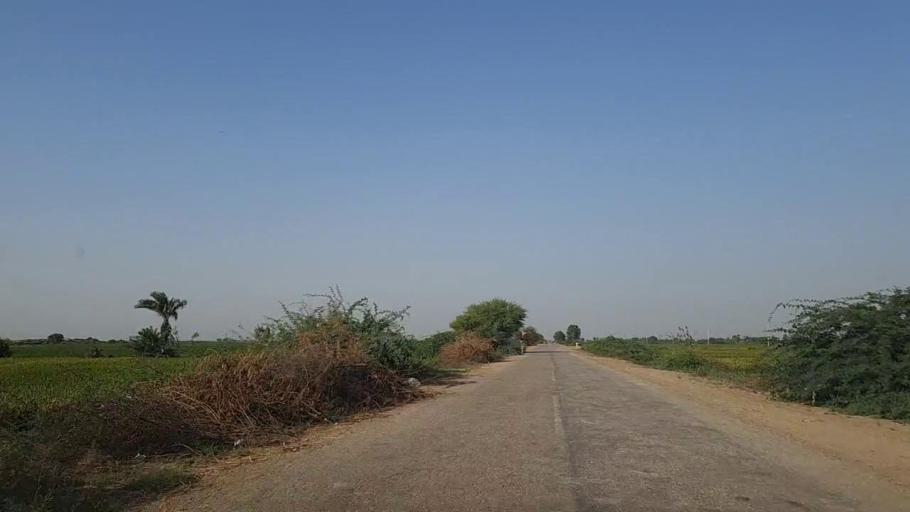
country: PK
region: Sindh
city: Mirpur Batoro
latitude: 24.5833
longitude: 68.3965
